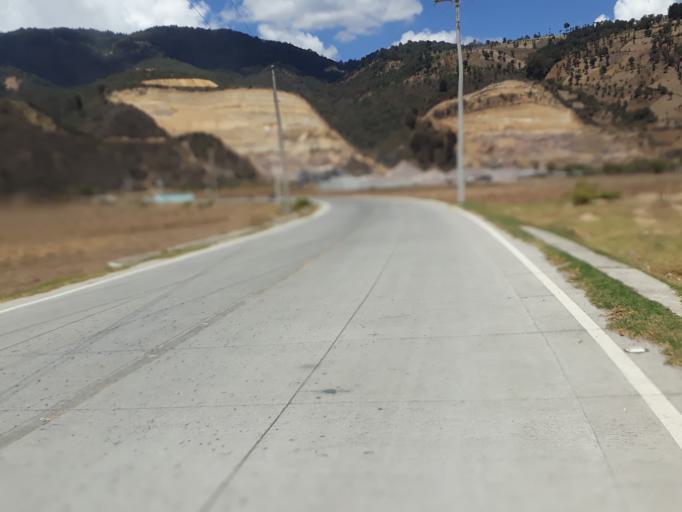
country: GT
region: Quetzaltenango
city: Quetzaltenango
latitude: 14.8151
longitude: -91.5504
